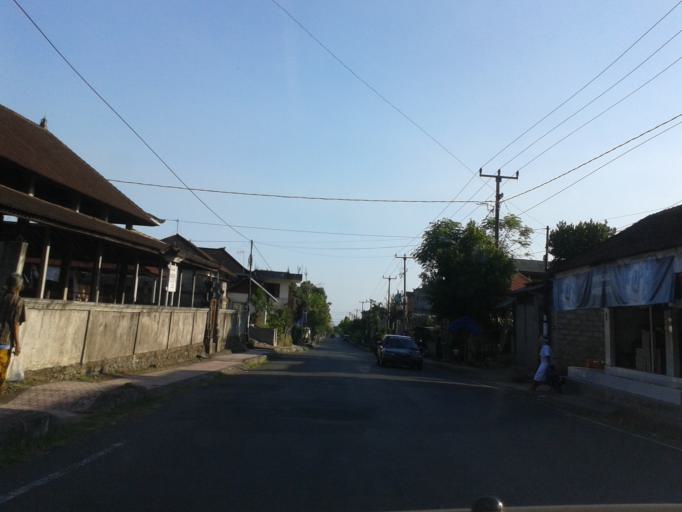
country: ID
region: Bali
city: Klungkung
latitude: -8.5114
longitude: 115.4019
